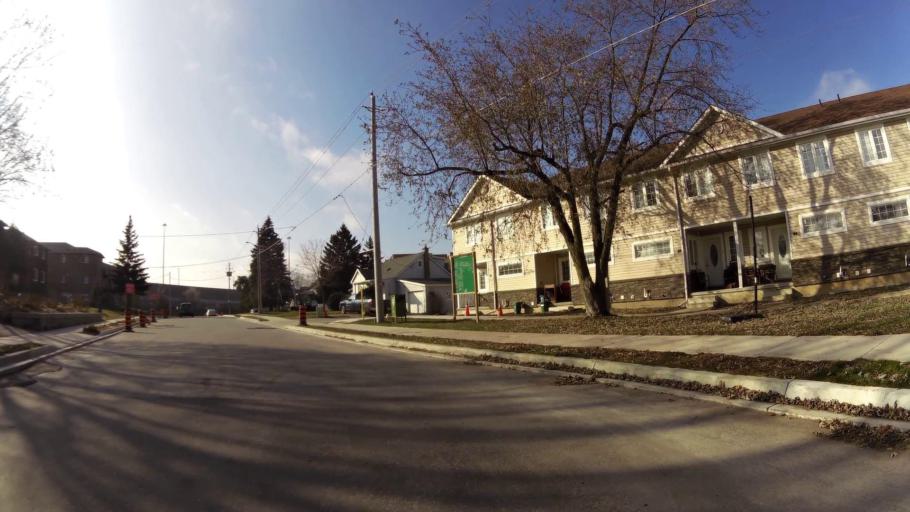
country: CA
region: Ontario
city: Kitchener
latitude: 43.4297
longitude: -80.4816
